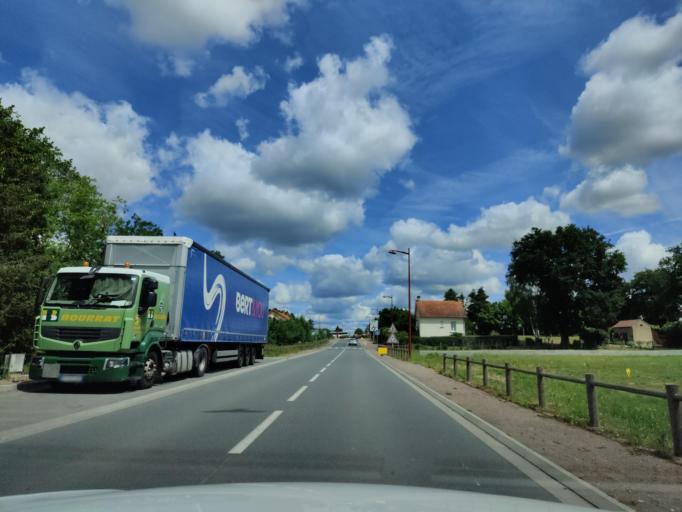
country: FR
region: Auvergne
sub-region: Departement de l'Allier
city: Saint-Victor
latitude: 46.3974
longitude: 2.6096
